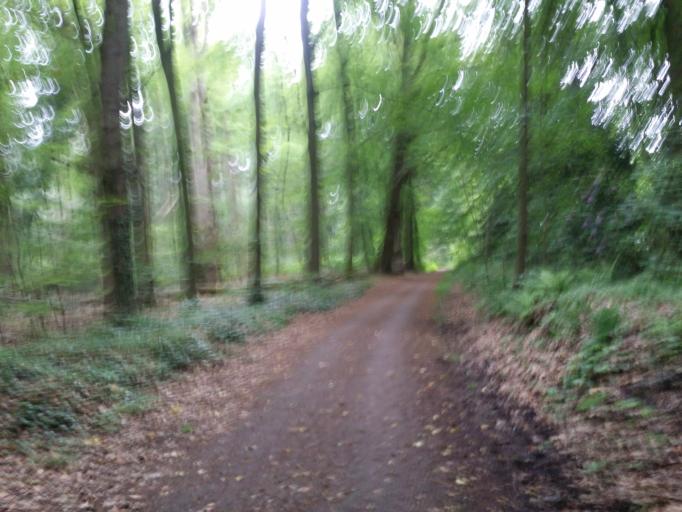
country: DE
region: Lower Saxony
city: Rastede
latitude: 53.2379
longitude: 8.2244
